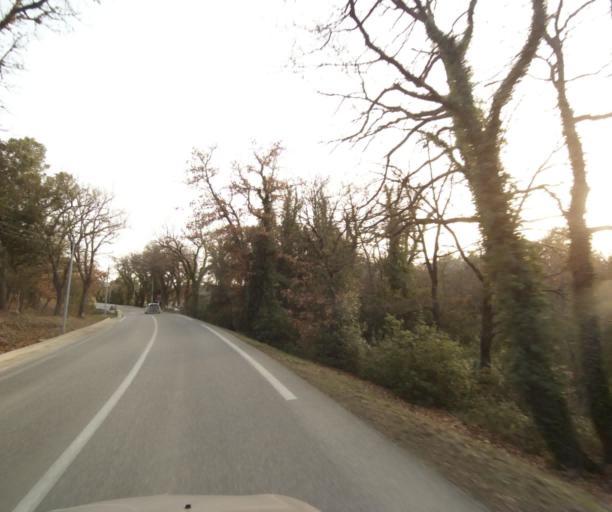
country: FR
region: Provence-Alpes-Cote d'Azur
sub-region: Departement des Bouches-du-Rhone
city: Rognes
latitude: 43.6412
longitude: 5.3589
